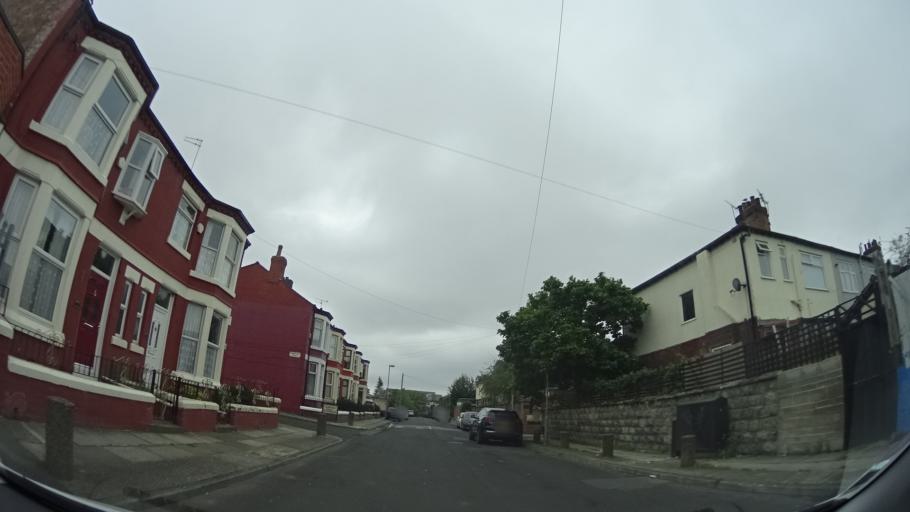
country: GB
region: England
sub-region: Liverpool
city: Liverpool
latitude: 53.4120
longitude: -2.9421
